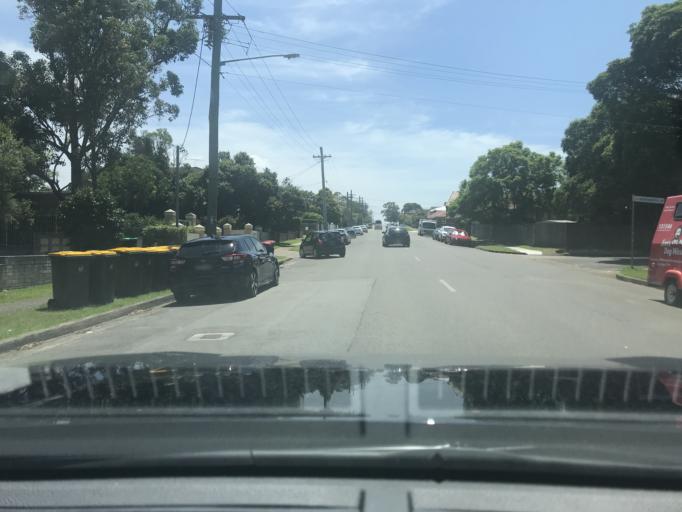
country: AU
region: New South Wales
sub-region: Canada Bay
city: Concord
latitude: -33.8627
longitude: 151.1006
